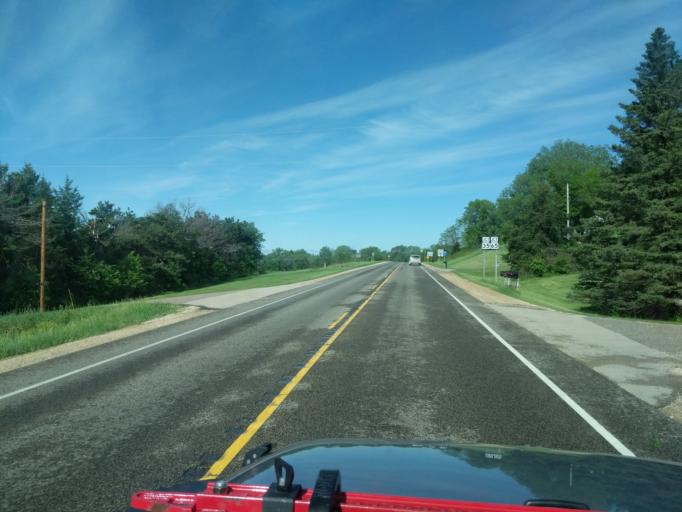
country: US
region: Wisconsin
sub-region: Pierce County
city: River Falls
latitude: 44.8499
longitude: -92.5993
